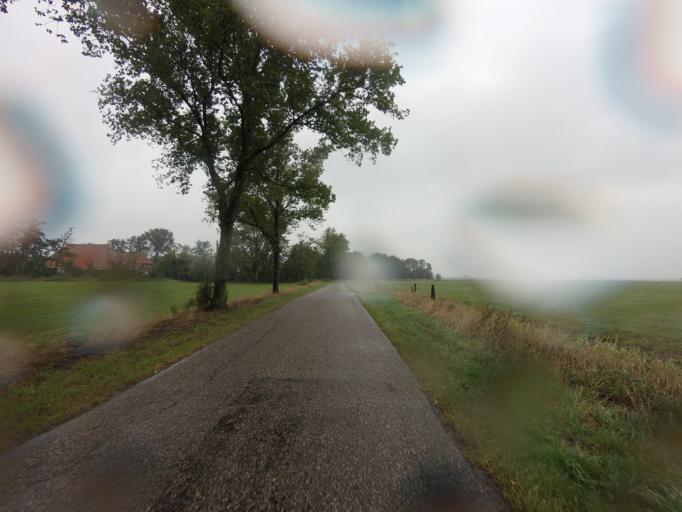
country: NL
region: Friesland
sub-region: Gemeente Boarnsterhim
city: Aldeboarn
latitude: 53.0731
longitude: 5.9286
